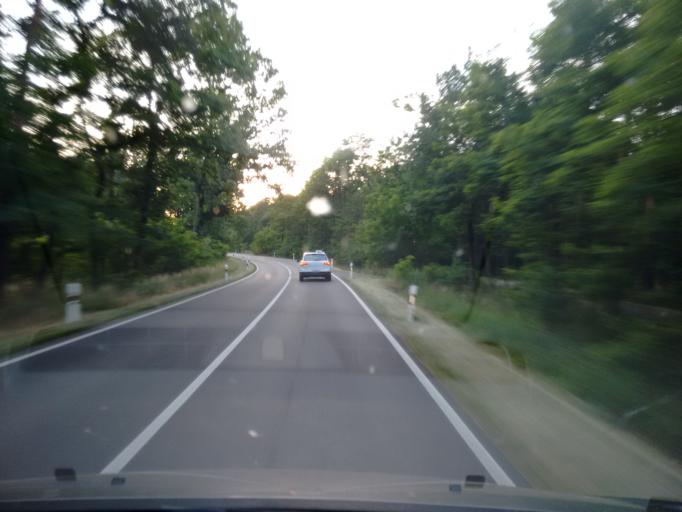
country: DE
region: Brandenburg
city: Mixdorf
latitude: 52.1669
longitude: 14.3726
